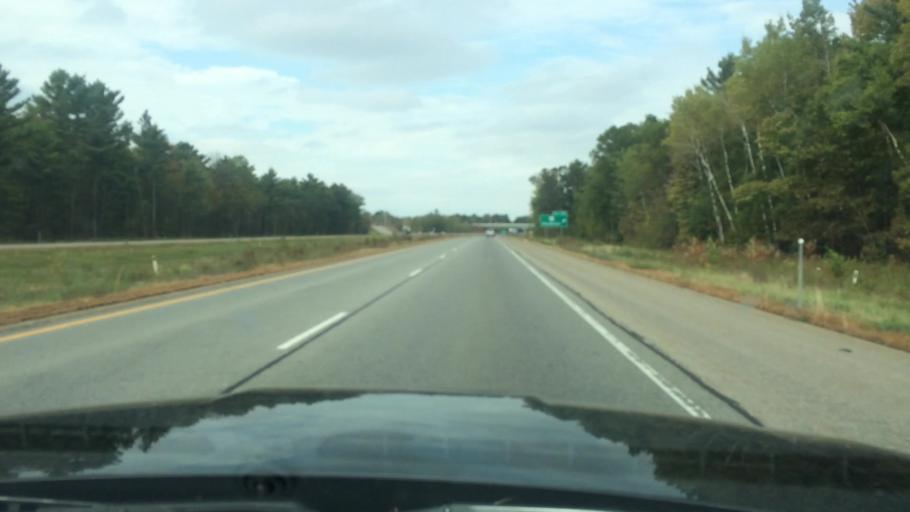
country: US
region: Wisconsin
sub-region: Marathon County
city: Mosinee
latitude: 44.7241
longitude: -89.6723
